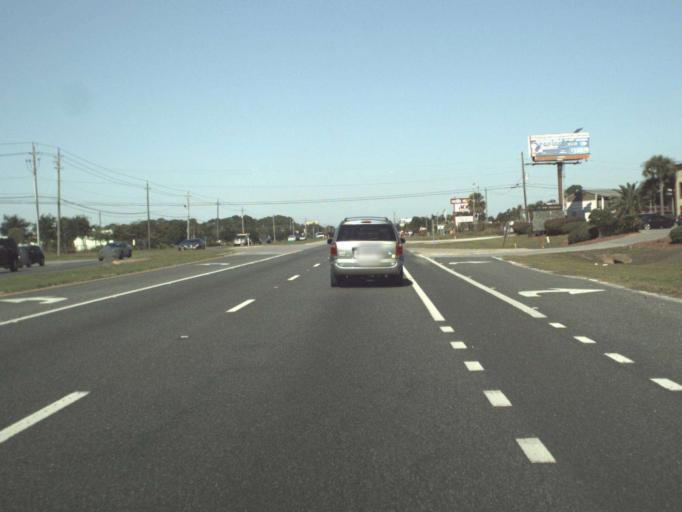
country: US
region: Florida
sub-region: Bay County
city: Laguna Beach
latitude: 30.2374
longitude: -85.9066
